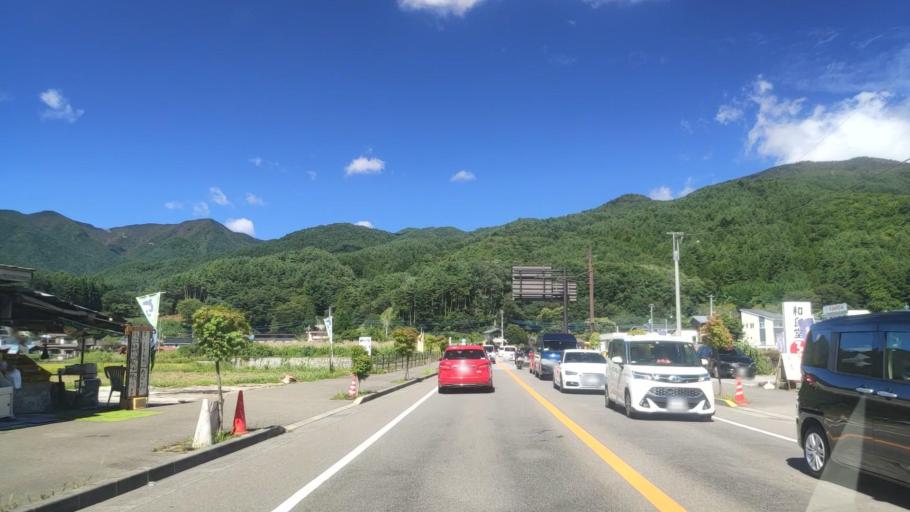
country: JP
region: Yamanashi
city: Fujikawaguchiko
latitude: 35.5225
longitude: 138.7775
